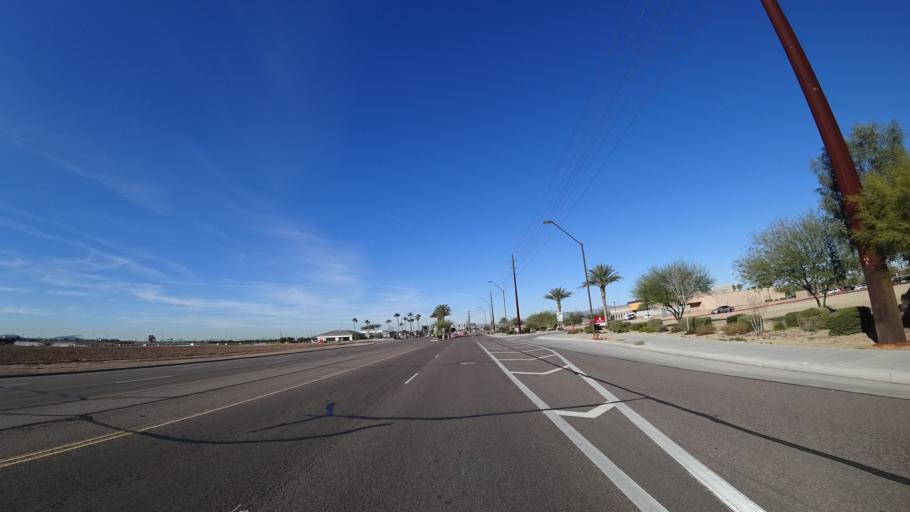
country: US
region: Arizona
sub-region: Maricopa County
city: Tolleson
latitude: 33.4642
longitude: -112.3036
